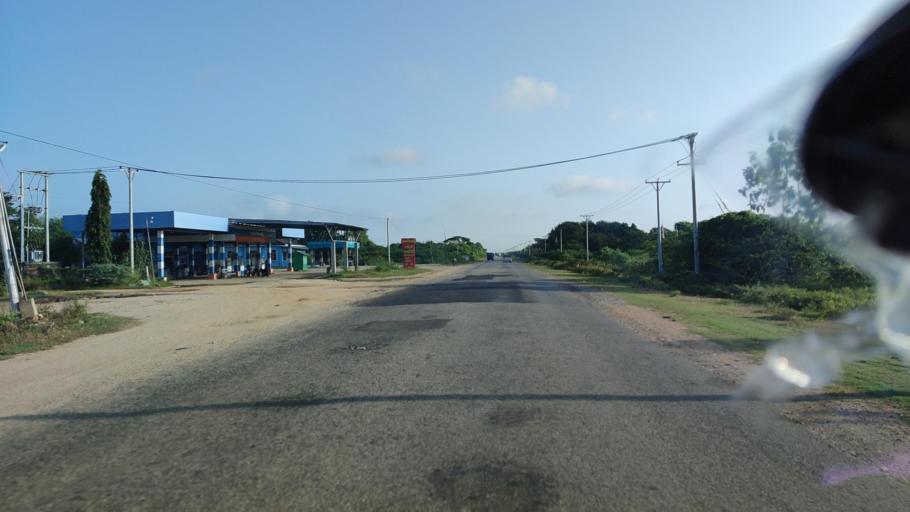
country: MM
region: Mandalay
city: Yamethin
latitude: 20.6122
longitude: 96.0727
